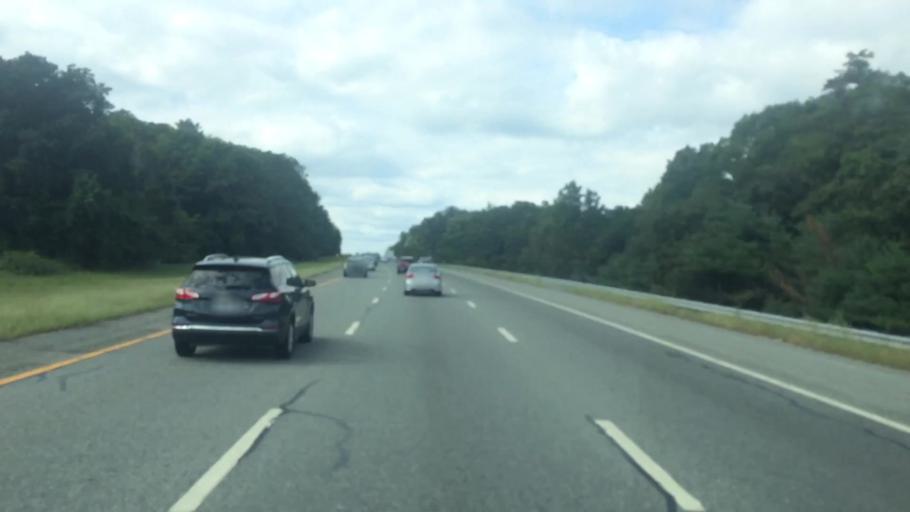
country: US
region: Rhode Island
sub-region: Providence County
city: Greenville
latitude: 41.8806
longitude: -71.5158
